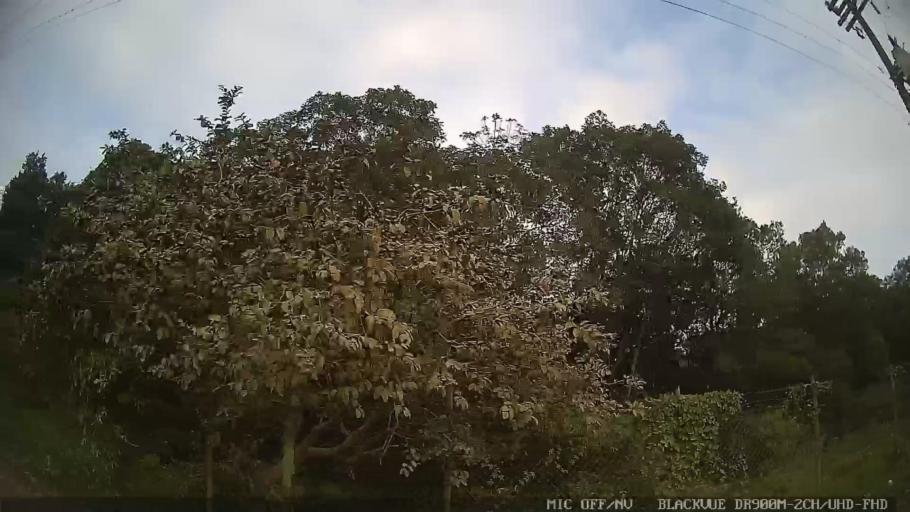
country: BR
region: Sao Paulo
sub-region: Guaruja
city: Guaruja
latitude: -23.9706
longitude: -46.2155
